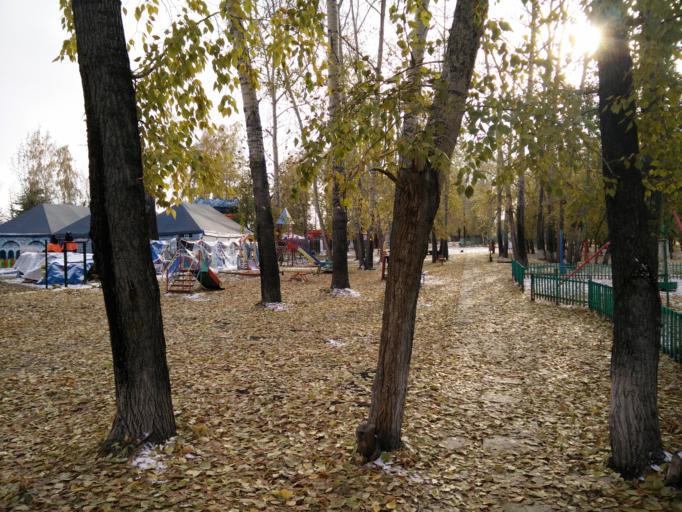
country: RU
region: Novosibirsk
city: Berdsk
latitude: 54.7591
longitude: 83.1029
